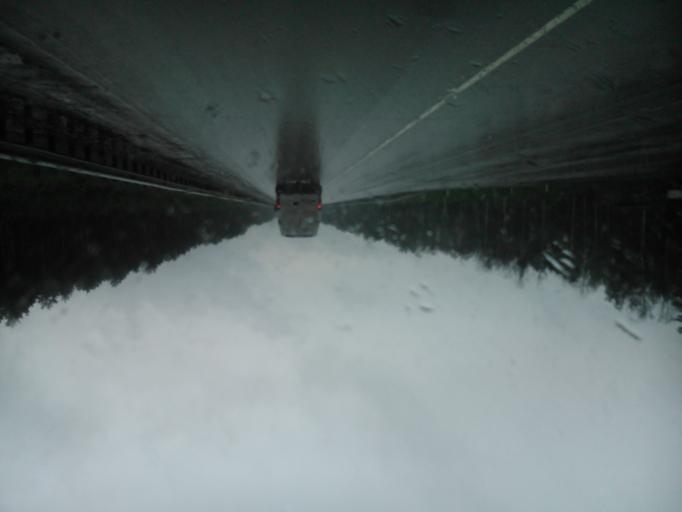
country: RU
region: Sverdlovsk
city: Shuvakish
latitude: 56.8896
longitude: 60.4111
